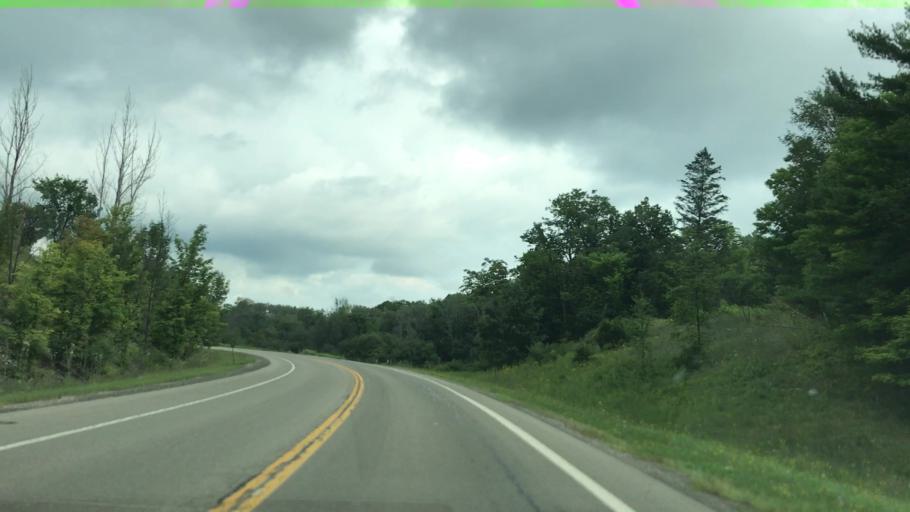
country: US
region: New York
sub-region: Steuben County
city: Bath
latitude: 42.3921
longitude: -77.3485
